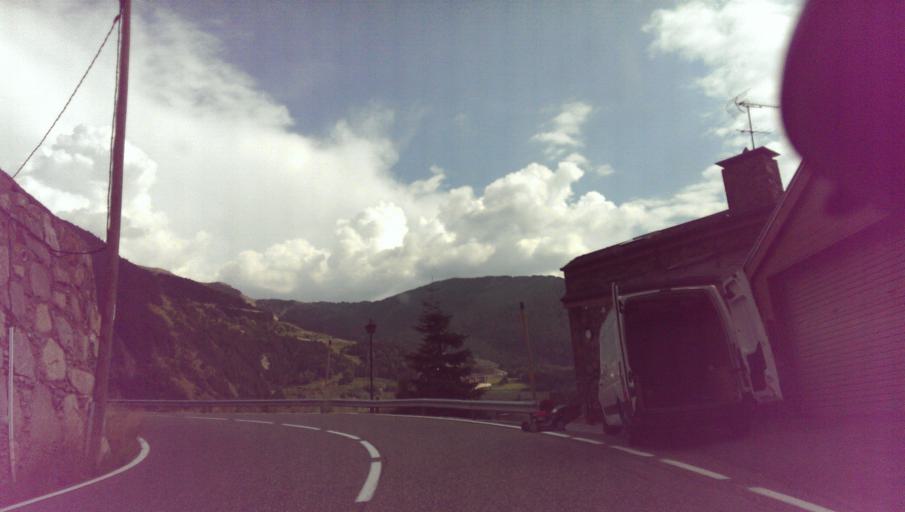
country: AD
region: Canillo
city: Canillo
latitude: 42.5691
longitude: 1.5986
